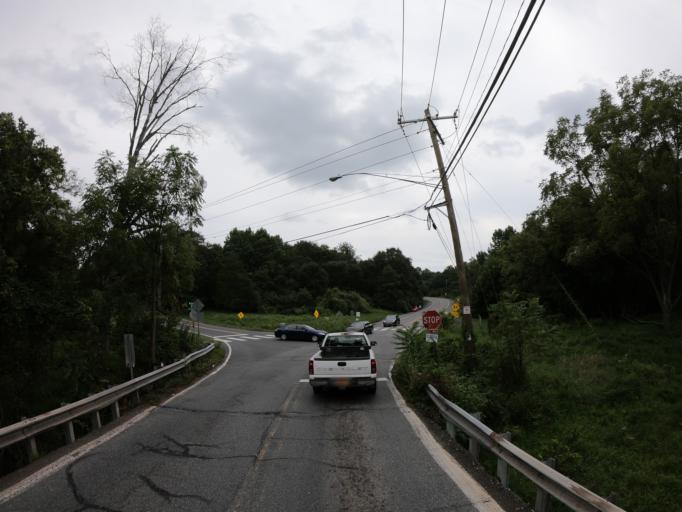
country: US
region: Maryland
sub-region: Montgomery County
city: Montgomery Village
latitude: 39.2013
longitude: -77.2040
